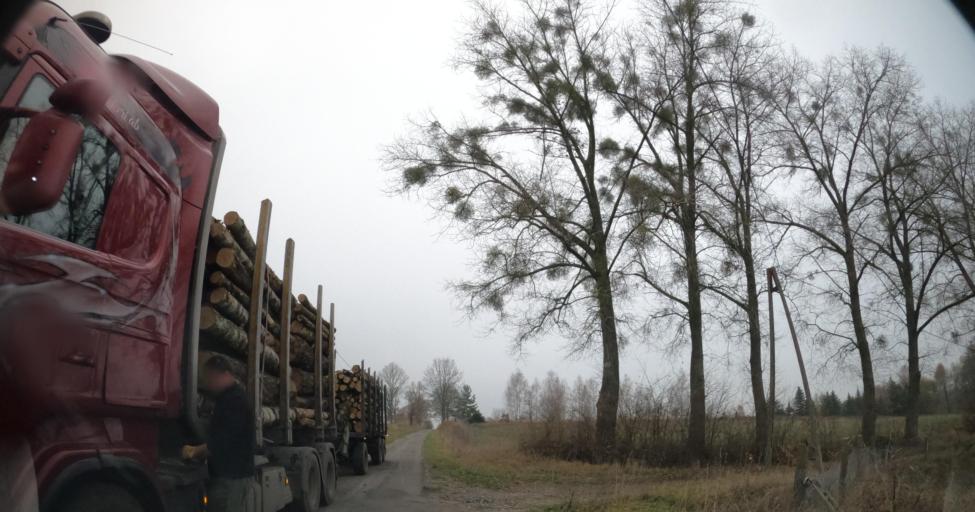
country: PL
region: West Pomeranian Voivodeship
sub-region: Powiat drawski
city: Drawsko Pomorskie
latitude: 53.5721
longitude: 15.8335
